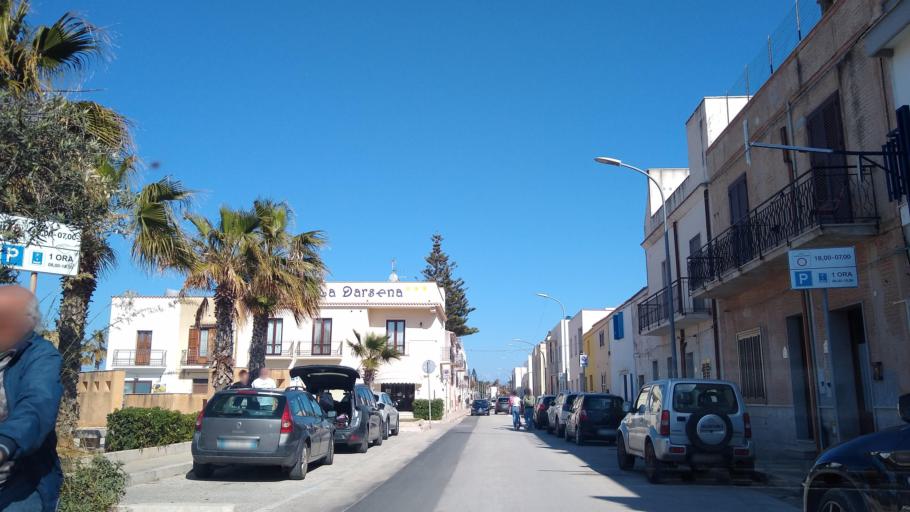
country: IT
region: Sicily
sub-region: Trapani
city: San Vito Lo Capo
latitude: 38.1751
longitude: 12.7371
